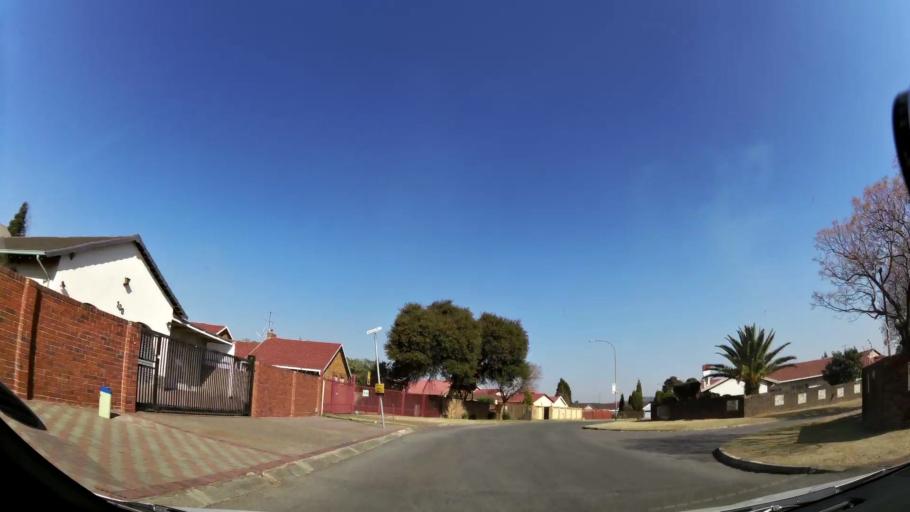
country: ZA
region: Gauteng
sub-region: City of Johannesburg Metropolitan Municipality
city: Johannesburg
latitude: -26.2594
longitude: 27.9964
